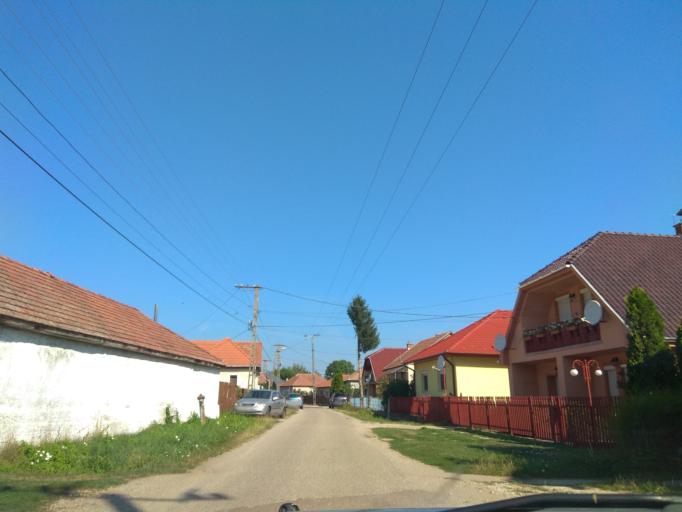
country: HU
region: Borsod-Abauj-Zemplen
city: Harsany
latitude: 47.9829
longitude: 20.7831
